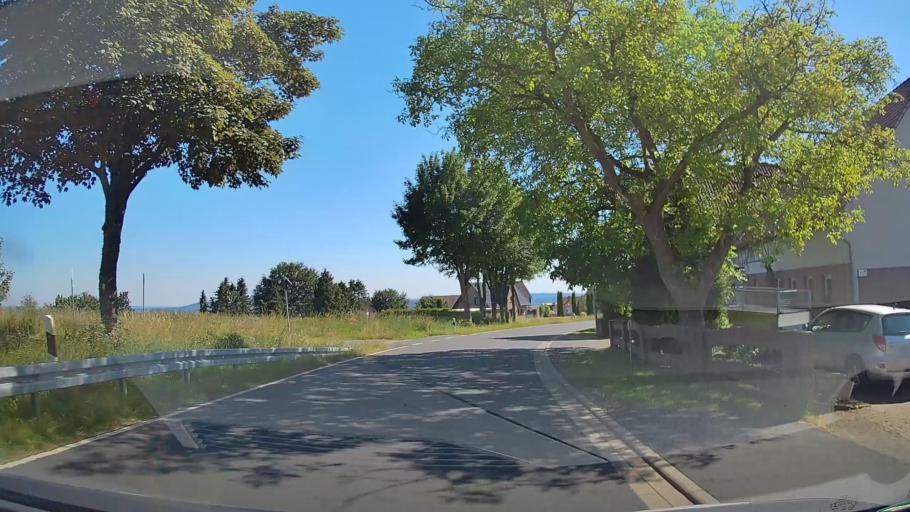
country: DE
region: North Rhine-Westphalia
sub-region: Regierungsbezirk Detmold
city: Lugde
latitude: 51.9526
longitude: 9.2983
